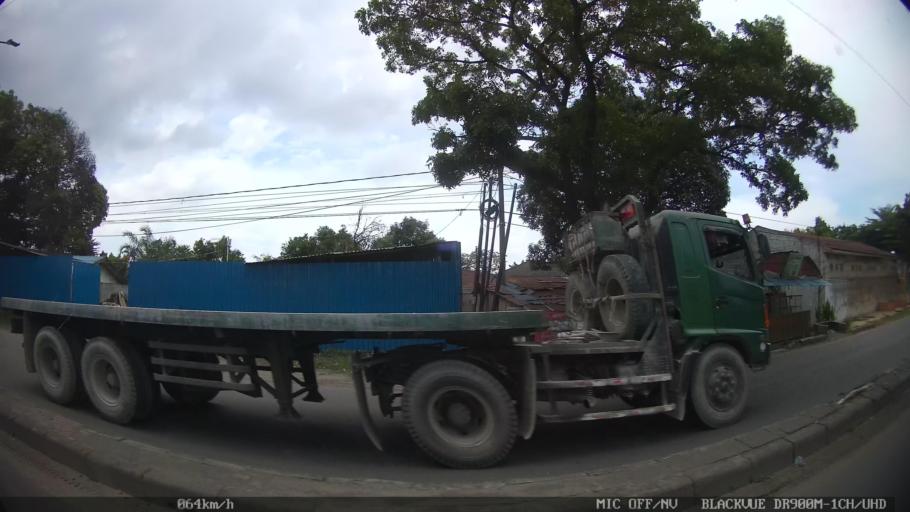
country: ID
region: North Sumatra
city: Labuhan Deli
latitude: 3.6911
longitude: 98.6706
